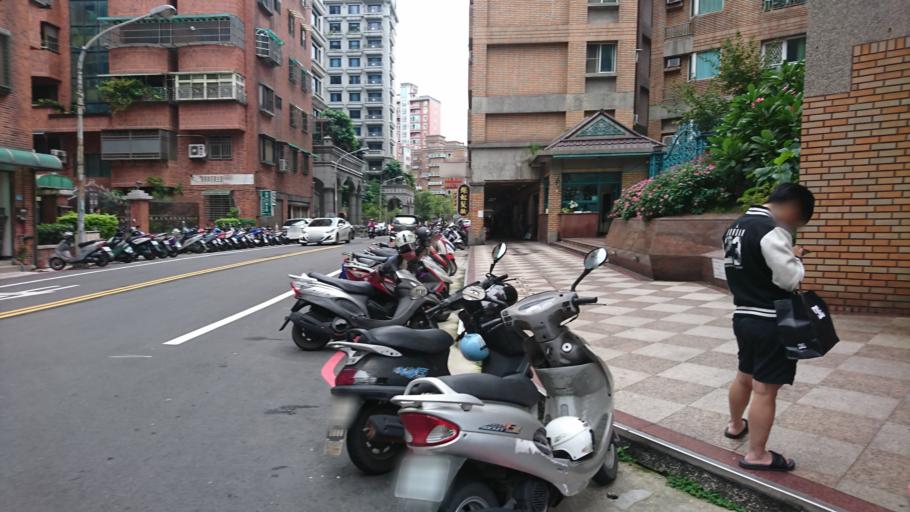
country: TW
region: Taiwan
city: Taoyuan City
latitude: 25.0578
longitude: 121.2960
